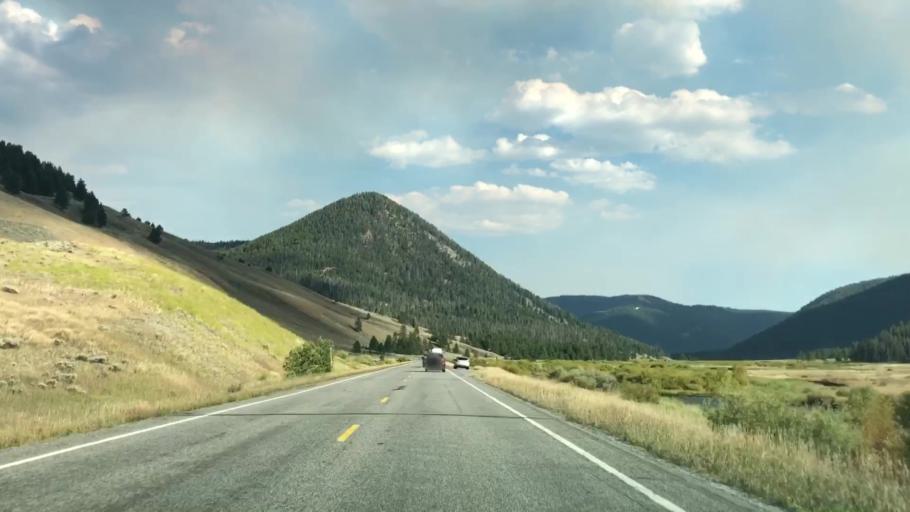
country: US
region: Montana
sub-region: Gallatin County
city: Big Sky
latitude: 45.0414
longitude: -111.1267
